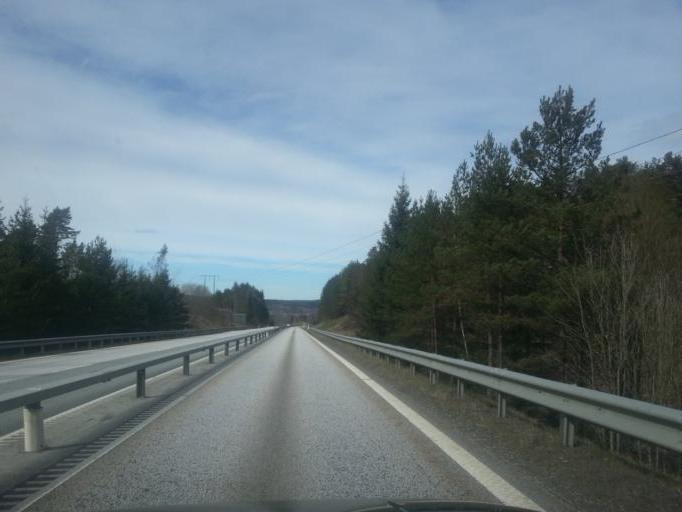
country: SE
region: Joenkoeping
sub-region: Jonkopings Kommun
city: Bankeryd
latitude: 57.7949
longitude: 14.0996
